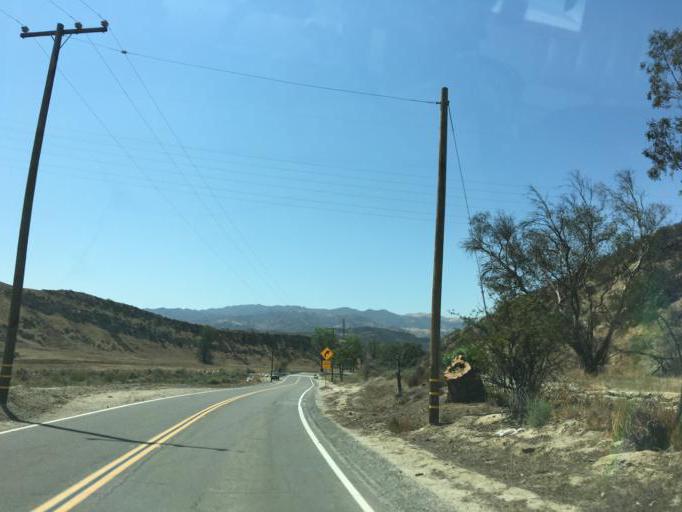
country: US
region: California
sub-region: Los Angeles County
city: Val Verde
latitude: 34.4257
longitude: -118.6577
